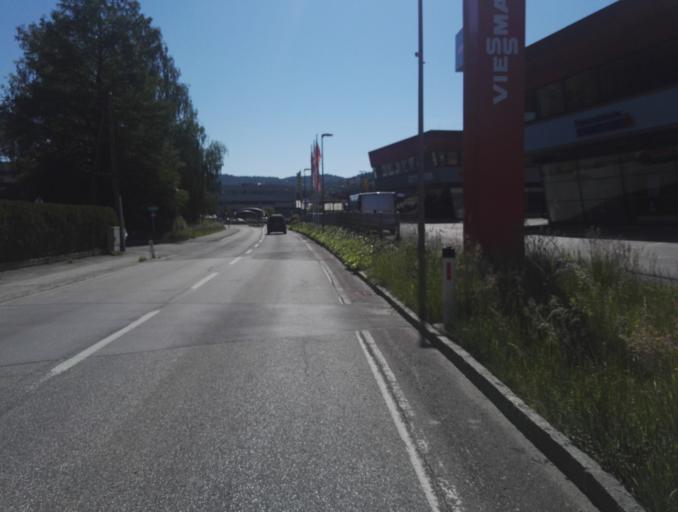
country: AT
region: Styria
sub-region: Politischer Bezirk Graz-Umgebung
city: Hart bei Graz
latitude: 47.0449
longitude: 15.5178
